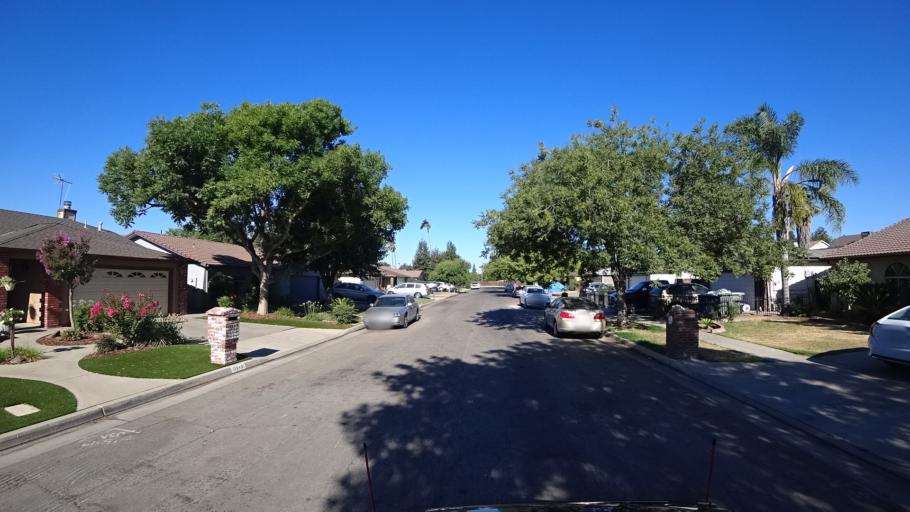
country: US
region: California
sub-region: Fresno County
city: West Park
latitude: 36.7824
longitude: -119.8565
